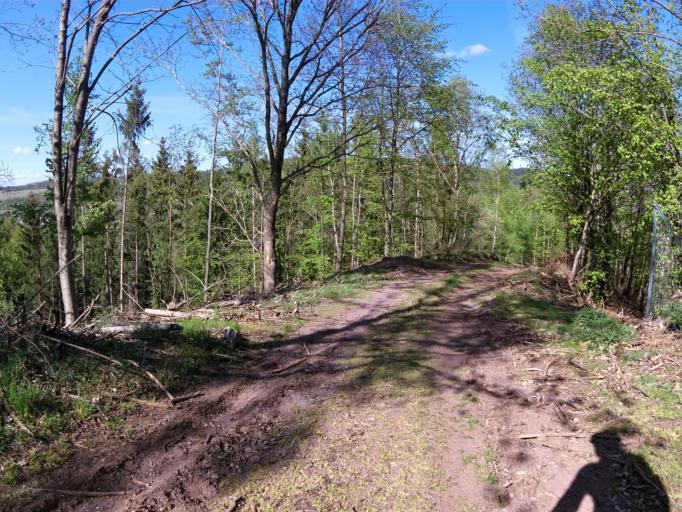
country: DE
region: Thuringia
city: Krauthausen
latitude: 50.9804
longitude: 10.2663
